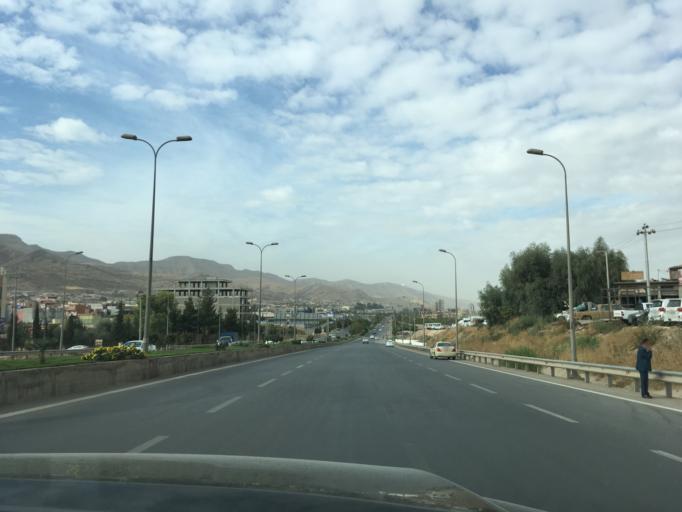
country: IQ
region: Dahuk
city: Sinah
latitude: 36.8496
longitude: 43.0467
